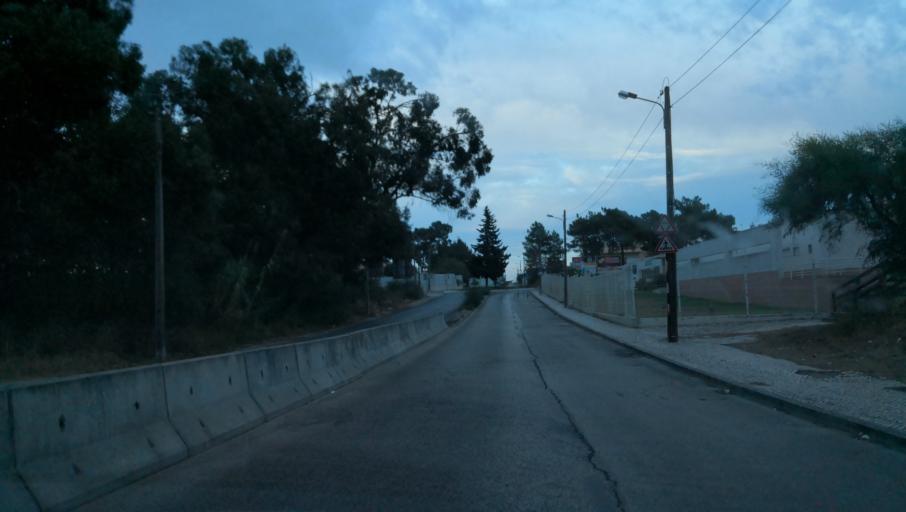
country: PT
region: Setubal
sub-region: Almada
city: Charneca
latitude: 38.6006
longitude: -9.1794
